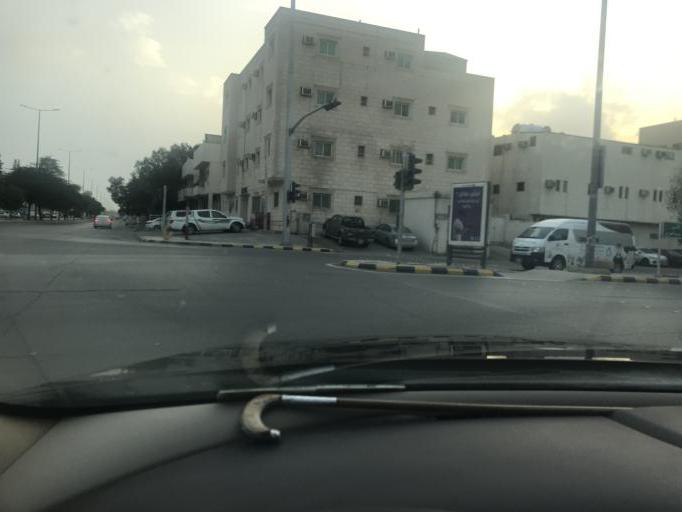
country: SA
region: Ar Riyad
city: Riyadh
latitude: 24.7275
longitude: 46.7650
